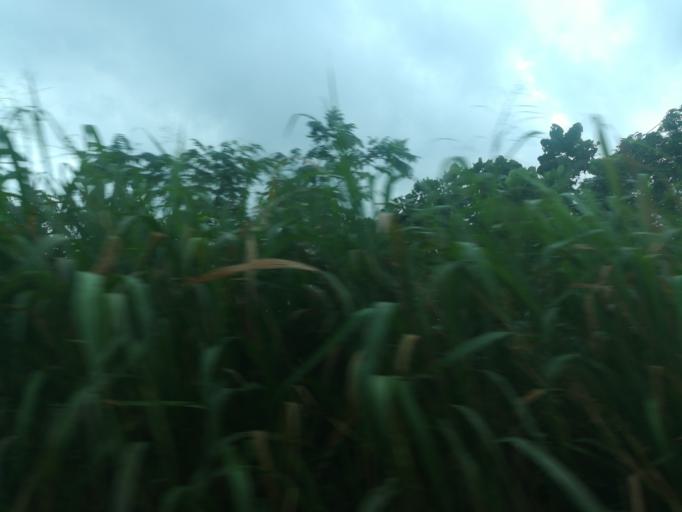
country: NG
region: Lagos
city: Ikorodu
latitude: 6.6641
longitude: 3.6011
